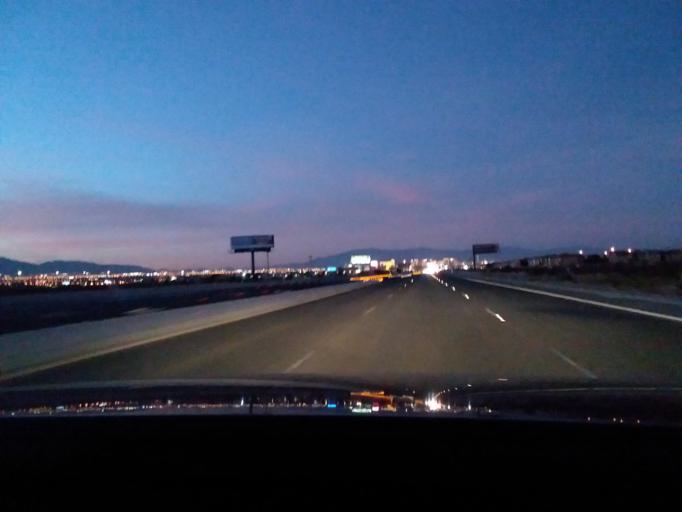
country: US
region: Nevada
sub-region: Clark County
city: Enterprise
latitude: 35.9680
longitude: -115.1727
